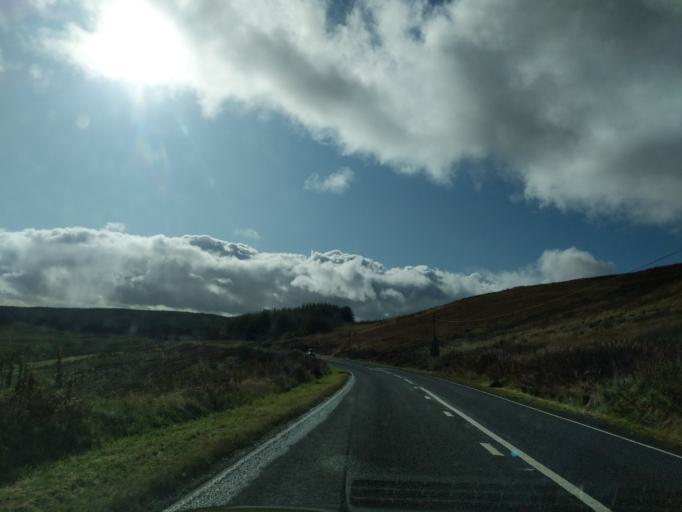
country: GB
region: Scotland
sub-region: Dumfries and Galloway
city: Moffat
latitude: 55.3929
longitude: -3.4819
